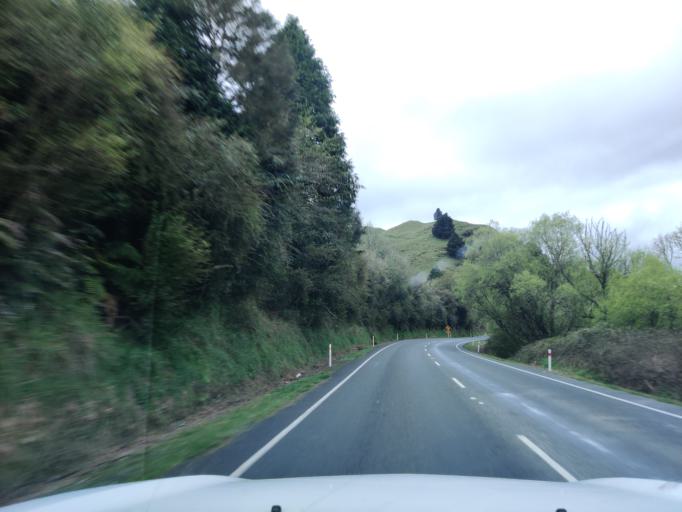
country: NZ
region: Waikato
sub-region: Otorohanga District
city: Otorohanga
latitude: -38.5998
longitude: 175.2171
